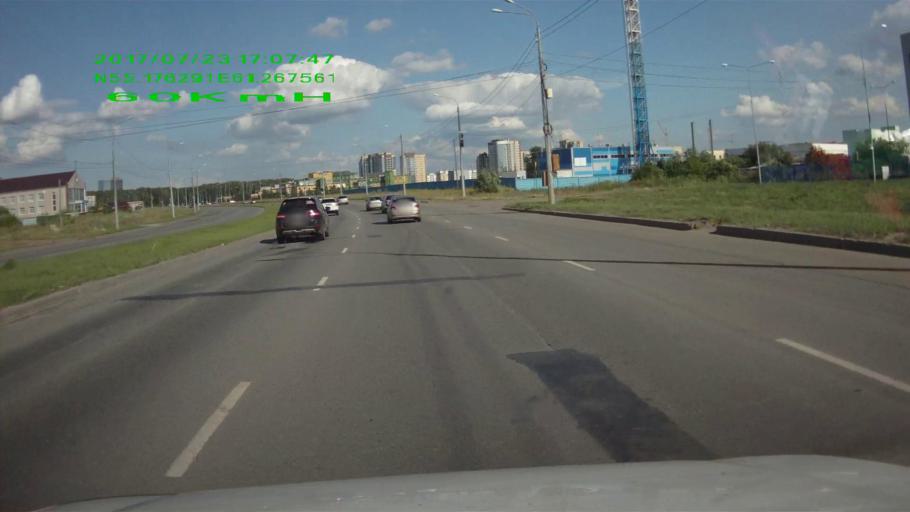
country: RU
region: Chelyabinsk
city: Roshchino
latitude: 55.1762
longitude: 61.2677
